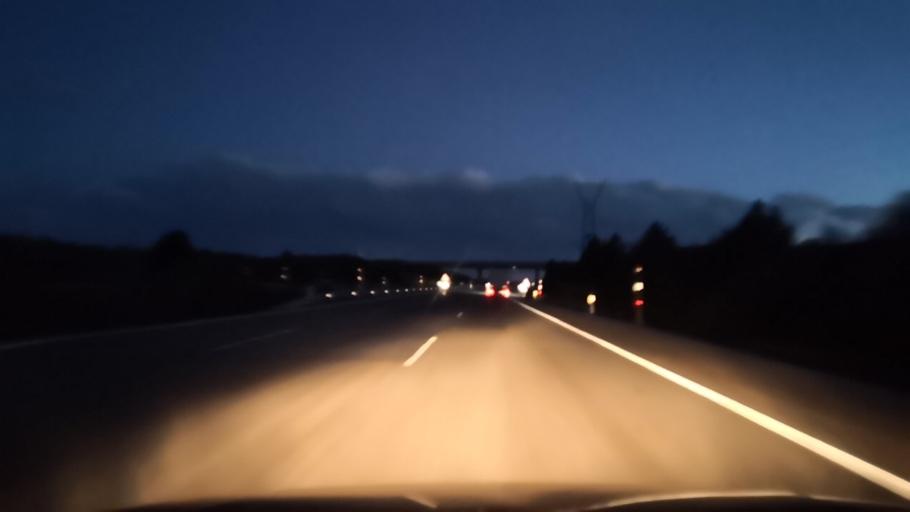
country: ES
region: Castille and Leon
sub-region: Provincia de Leon
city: Villagaton
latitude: 42.5819
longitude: -6.2155
